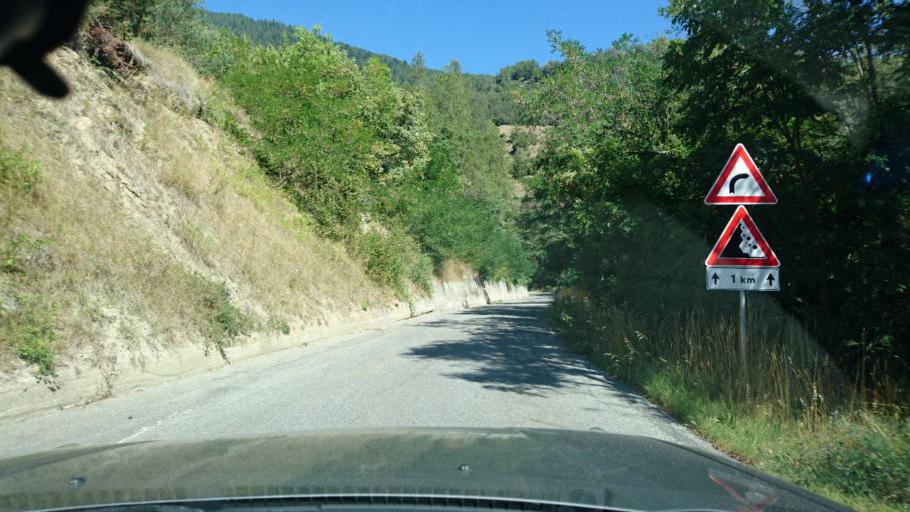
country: IT
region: Aosta Valley
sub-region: Valle d'Aosta
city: Ville Sur Sarre
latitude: 45.7373
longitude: 7.2647
